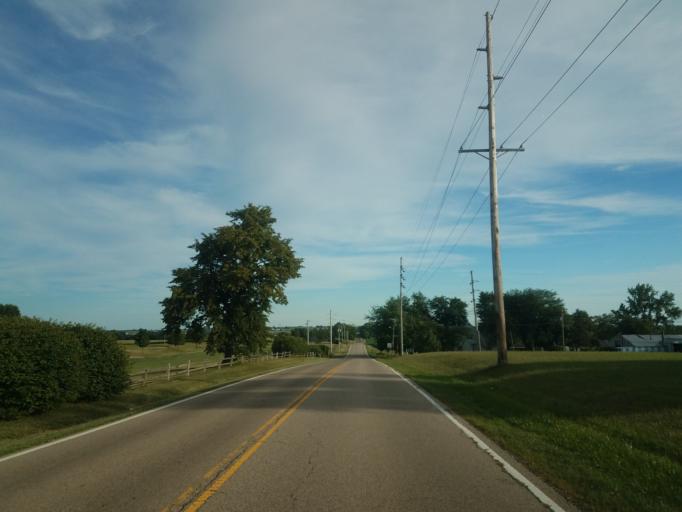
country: US
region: Illinois
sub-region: McLean County
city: Bloomington
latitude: 40.4454
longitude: -89.0056
